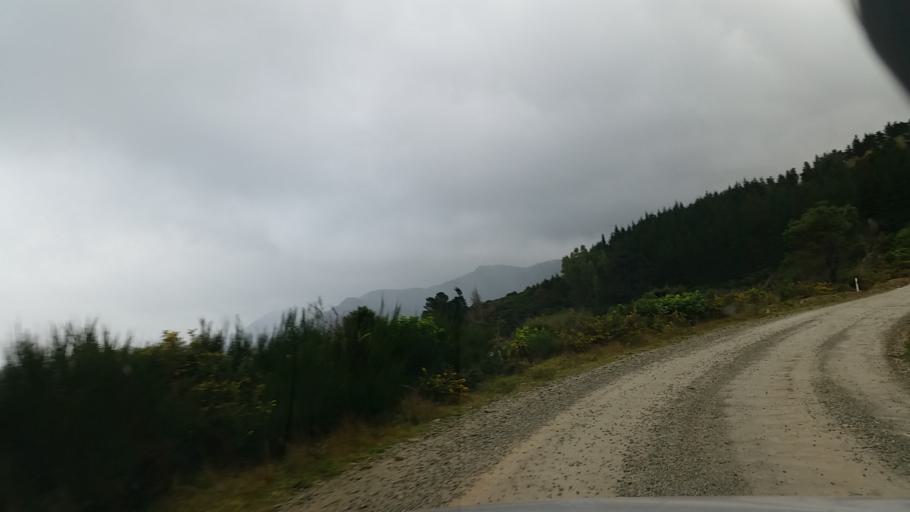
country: NZ
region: Marlborough
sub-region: Marlborough District
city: Picton
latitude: -41.1767
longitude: 174.0467
